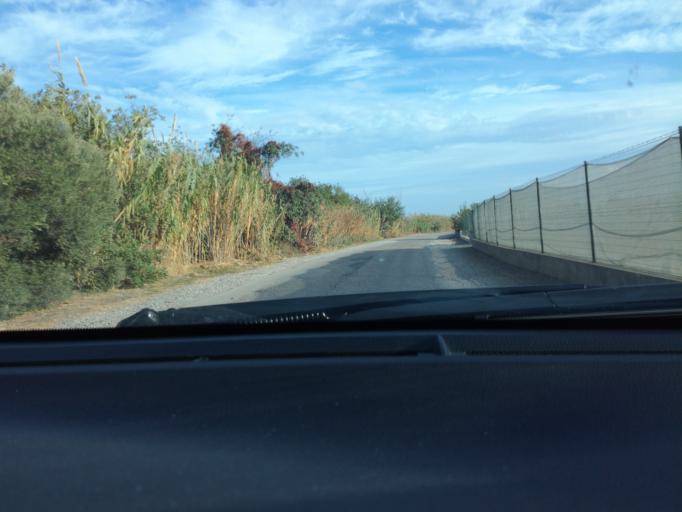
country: PT
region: Faro
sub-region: Olhao
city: Moncarapacho
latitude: 37.0737
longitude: -7.7706
